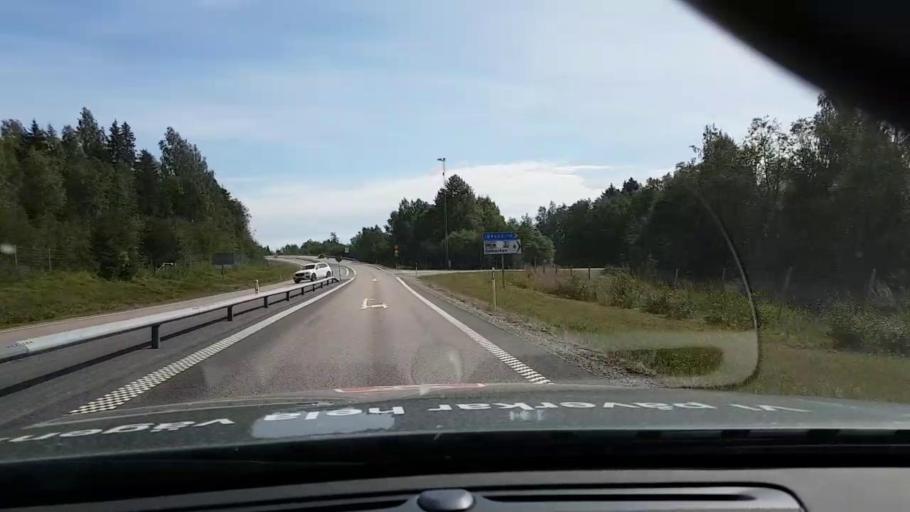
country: SE
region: Vaesternorrland
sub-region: OErnskoeldsviks Kommun
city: Ornskoldsvik
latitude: 63.2986
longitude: 18.8674
